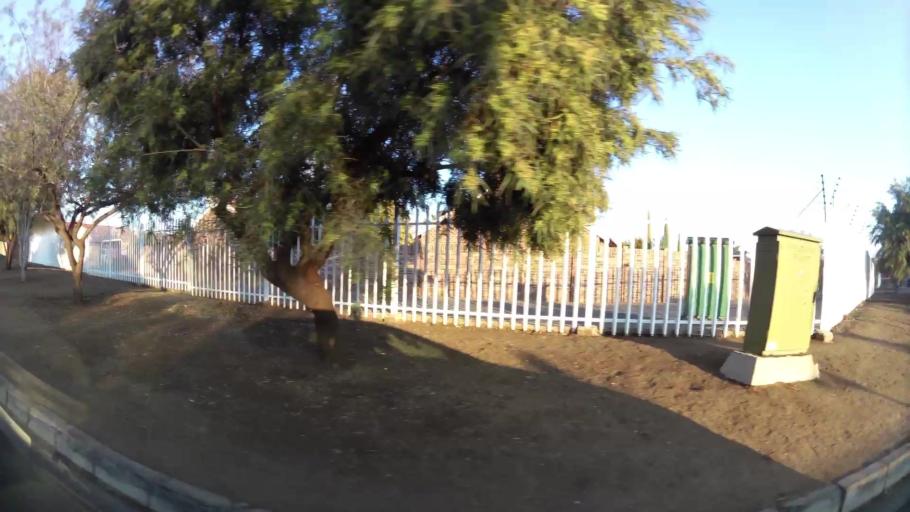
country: ZA
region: Orange Free State
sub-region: Mangaung Metropolitan Municipality
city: Bloemfontein
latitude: -29.0924
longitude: 26.1672
